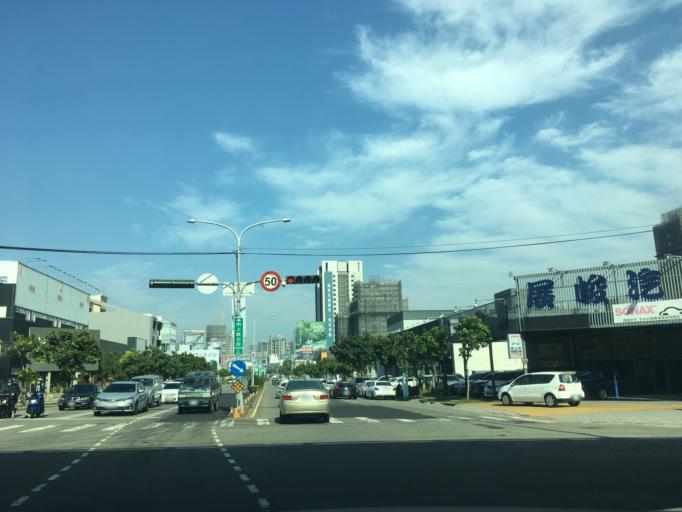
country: TW
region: Taiwan
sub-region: Taichung City
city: Taichung
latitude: 24.1453
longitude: 120.6232
